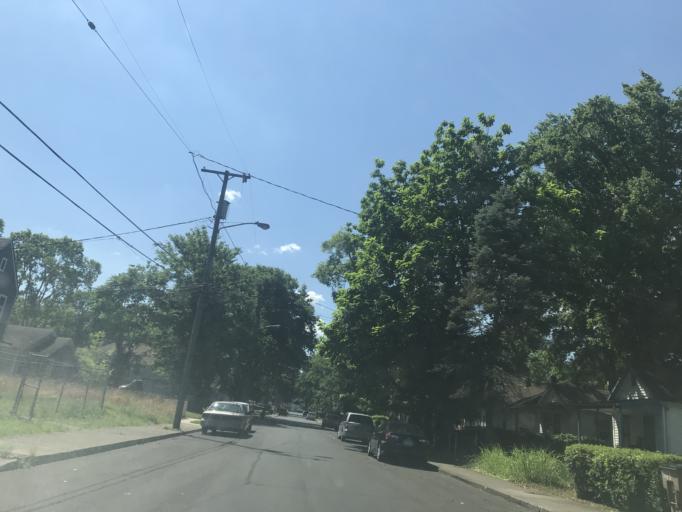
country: US
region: Tennessee
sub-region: Davidson County
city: Nashville
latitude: 36.1761
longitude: -86.8063
